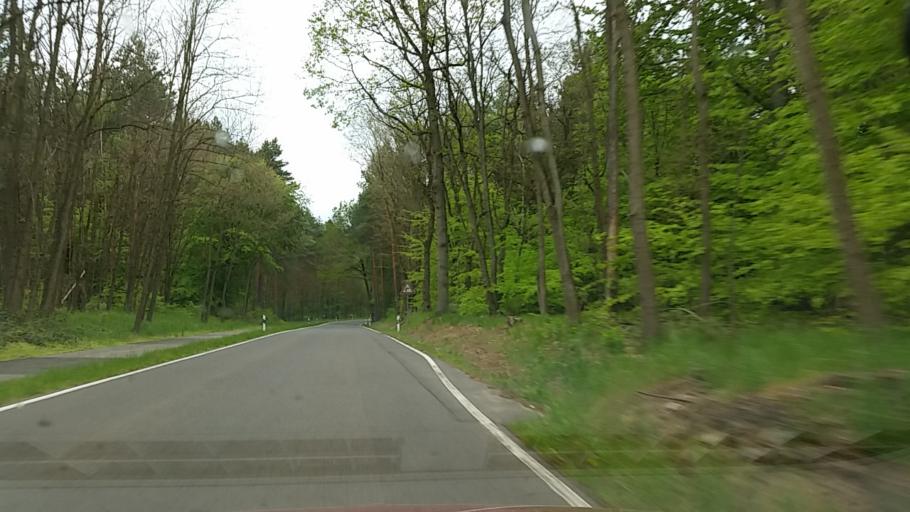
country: DE
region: Brandenburg
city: Reichenwalde
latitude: 52.3090
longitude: 13.9679
